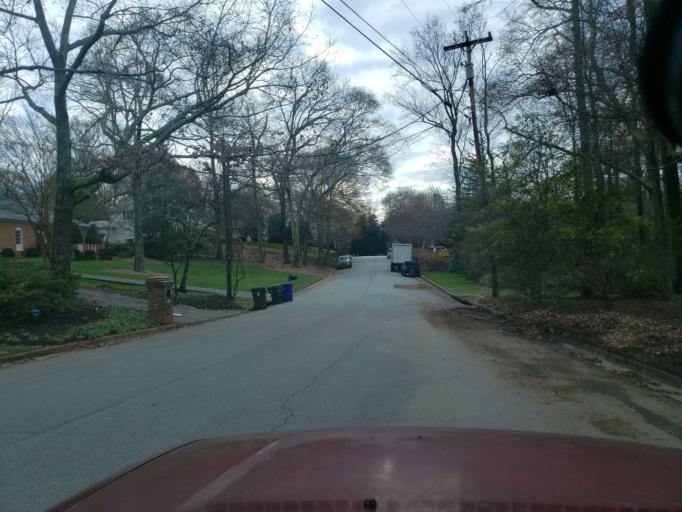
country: US
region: South Carolina
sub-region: Greenville County
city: Greenville
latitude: 34.8101
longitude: -82.3659
